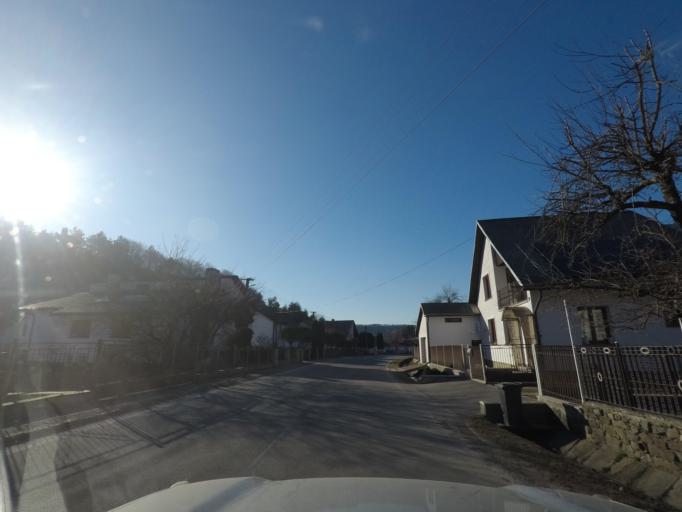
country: SK
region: Presovsky
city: Medzilaborce
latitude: 49.2475
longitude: 21.9294
